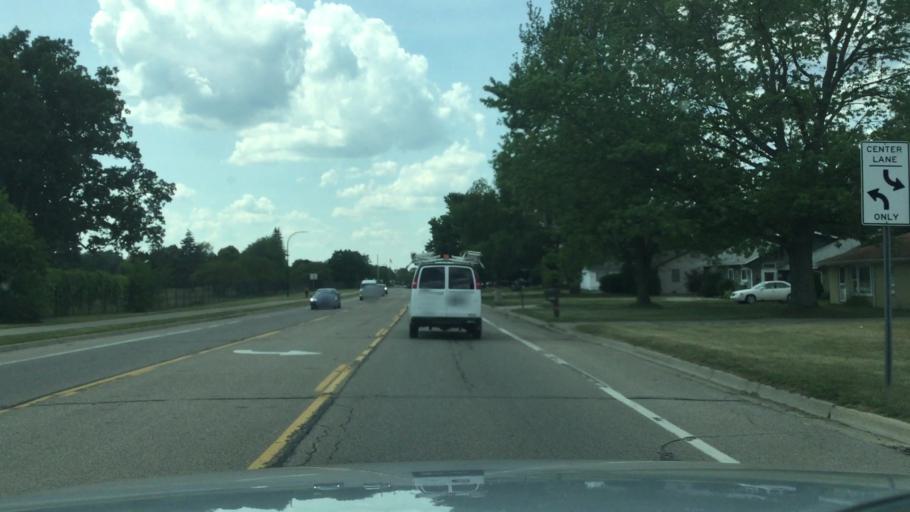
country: US
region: Michigan
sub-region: Washtenaw County
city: Ypsilanti
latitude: 42.2140
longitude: -83.5593
